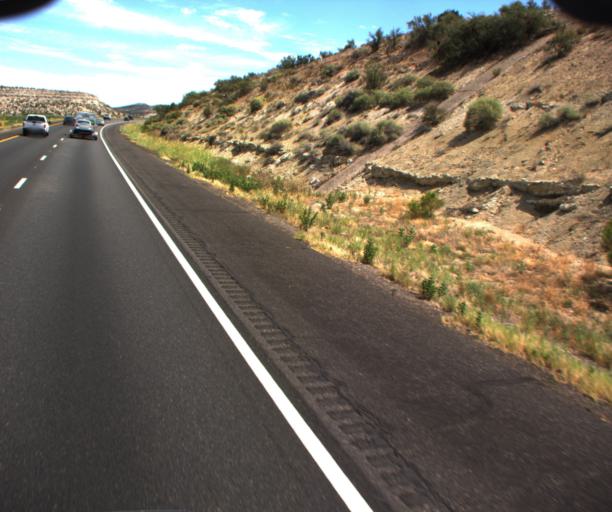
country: US
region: Arizona
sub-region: Yavapai County
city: Camp Verde
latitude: 34.6046
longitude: -111.8700
